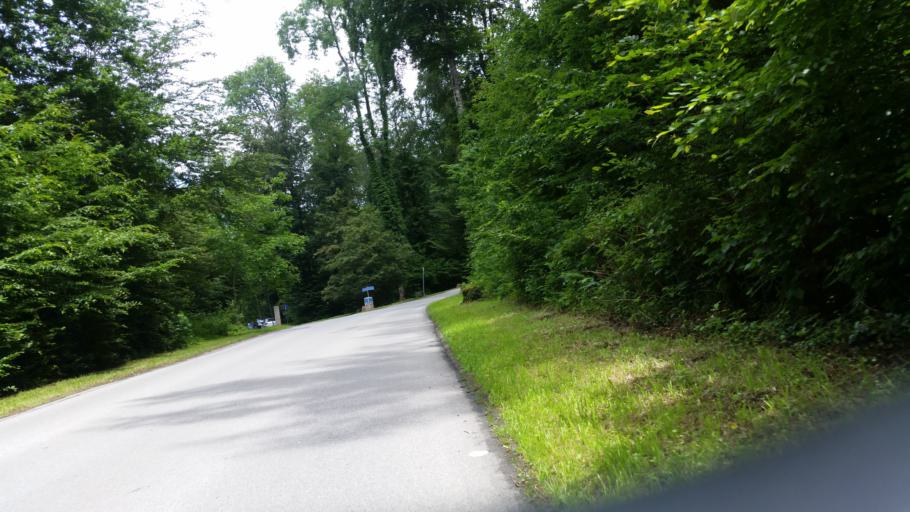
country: CH
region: Vaud
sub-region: Lausanne District
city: Romanel
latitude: 46.5755
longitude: 6.6188
